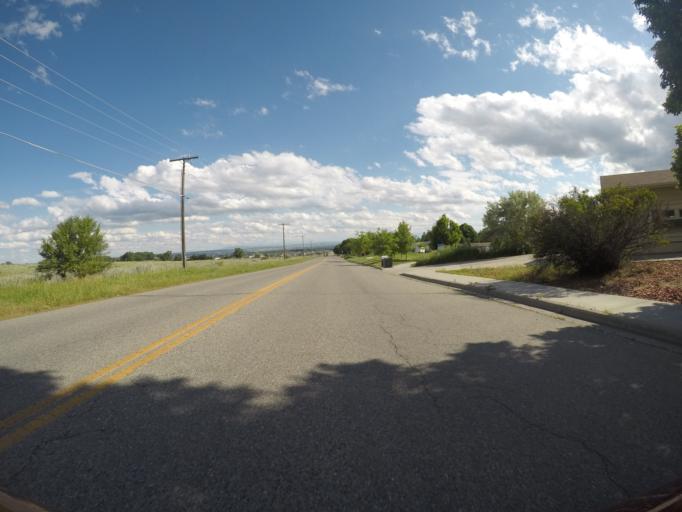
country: US
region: Montana
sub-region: Yellowstone County
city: Billings
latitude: 45.8032
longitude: -108.6527
